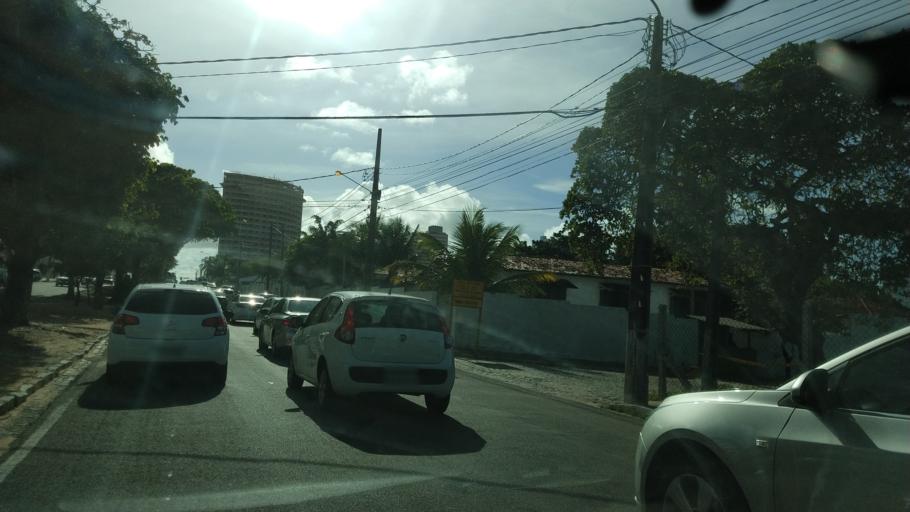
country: BR
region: Rio Grande do Norte
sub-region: Natal
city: Natal
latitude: -5.8083
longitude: -35.2007
